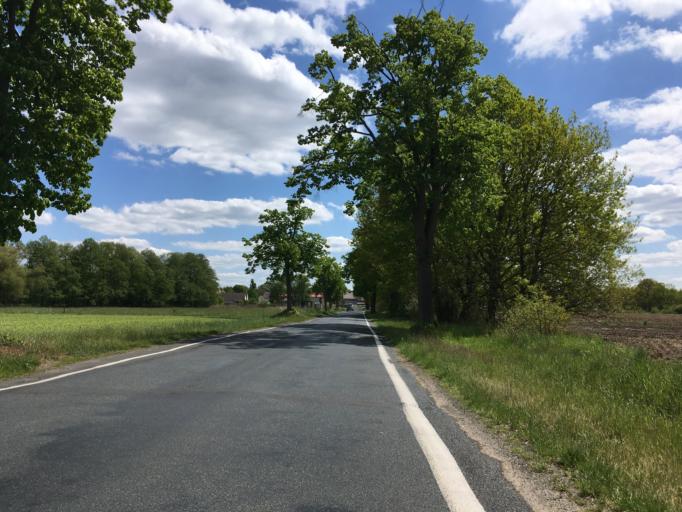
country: DE
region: Brandenburg
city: Wandlitz
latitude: 52.7799
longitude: 13.4334
